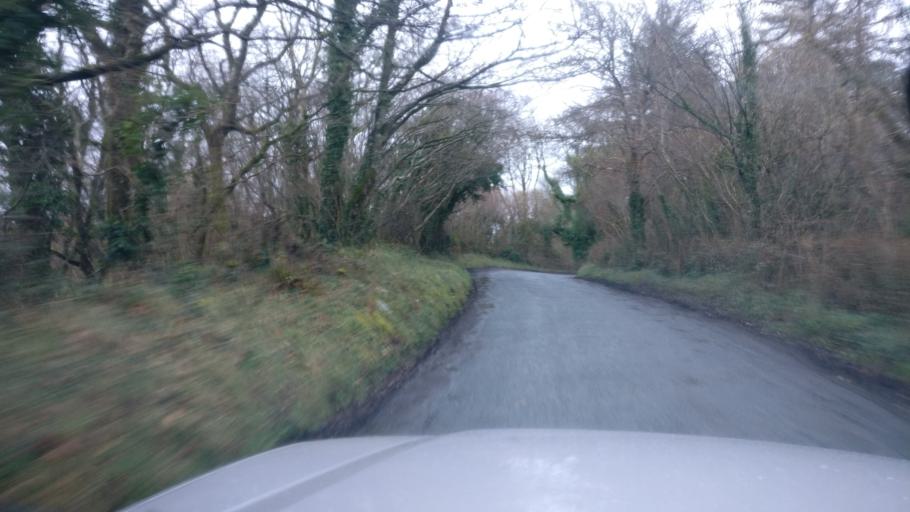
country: IE
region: Connaught
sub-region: County Galway
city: Ballinasloe
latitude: 53.2979
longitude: -8.2633
